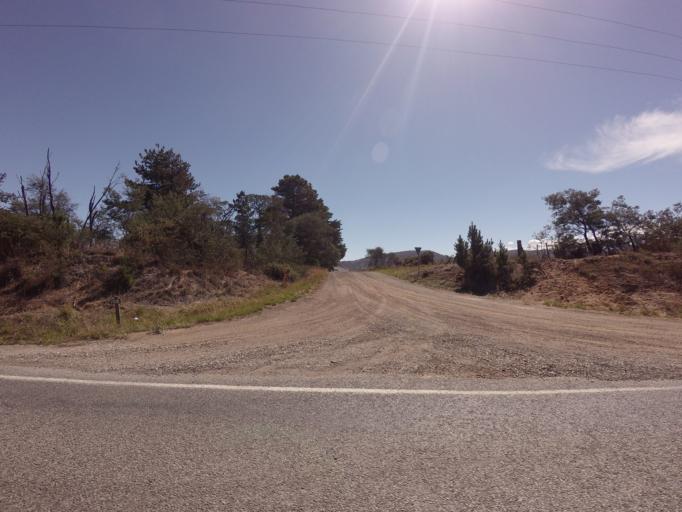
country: AU
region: Tasmania
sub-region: Northern Midlands
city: Evandale
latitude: -41.7860
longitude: 147.7163
